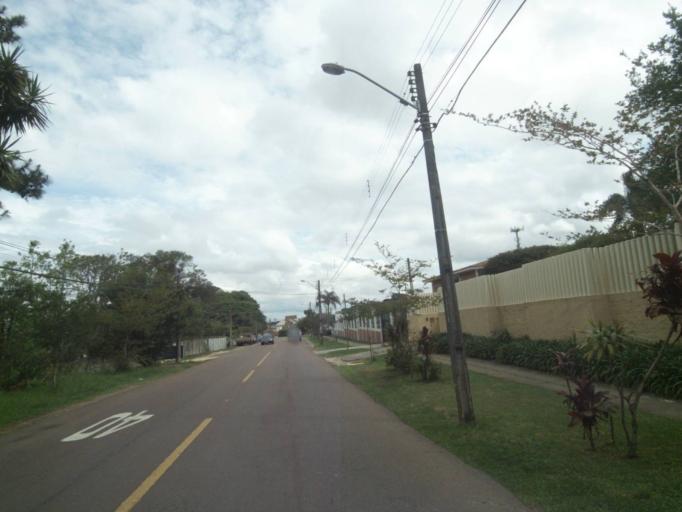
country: BR
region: Parana
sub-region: Curitiba
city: Curitiba
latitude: -25.3838
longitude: -49.2799
